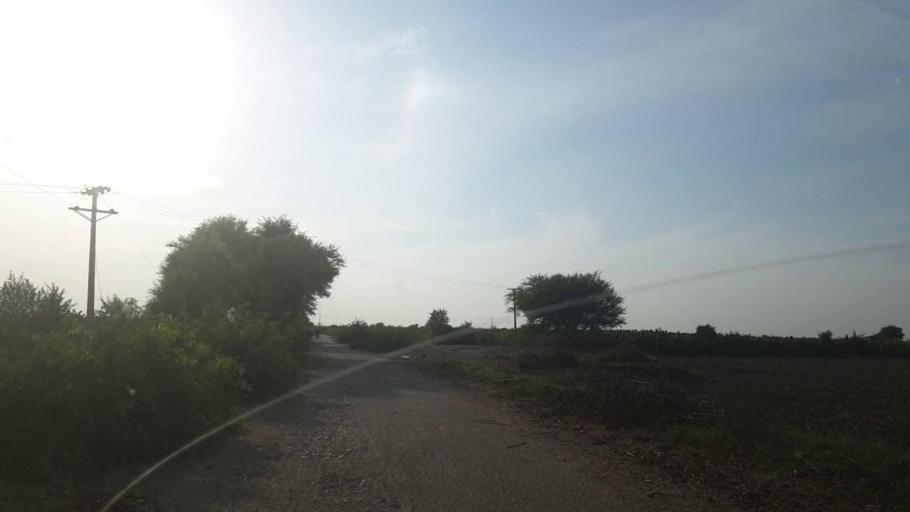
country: PK
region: Sindh
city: Tando Muhammad Khan
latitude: 25.2215
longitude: 68.5318
